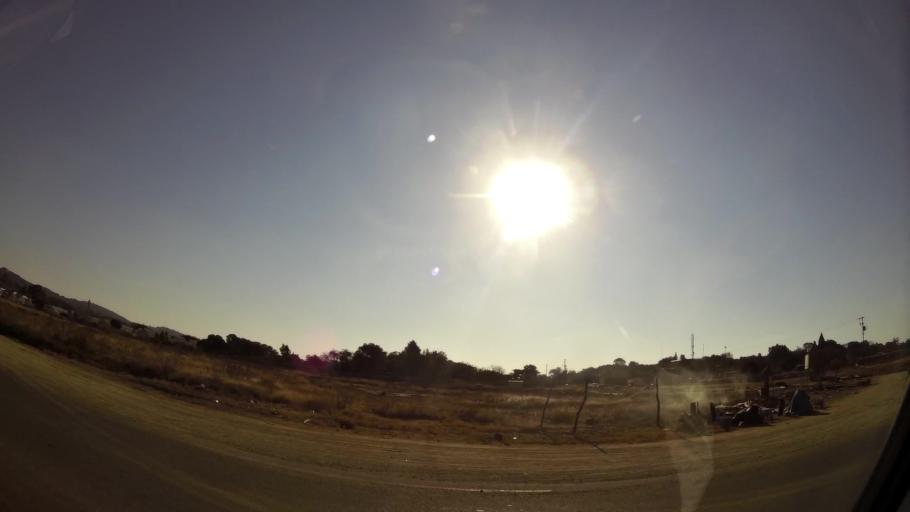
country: ZA
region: Gauteng
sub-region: City of Tshwane Metropolitan Municipality
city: Pretoria
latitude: -25.7718
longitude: 28.3531
